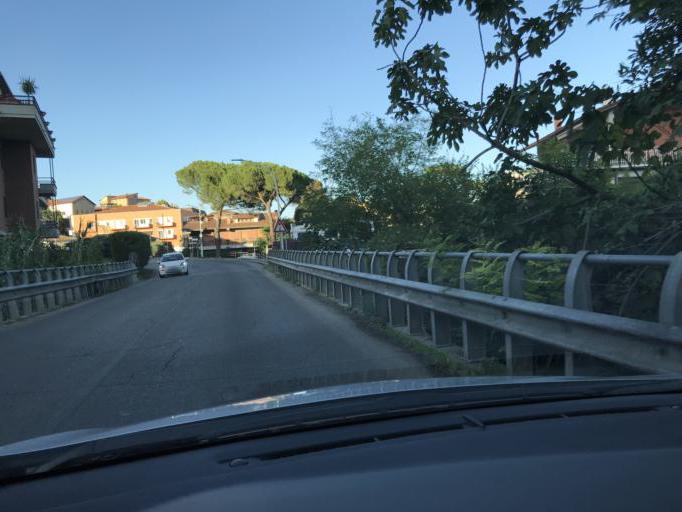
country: IT
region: Latium
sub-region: Provincia di Viterbo
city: Orte
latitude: 42.4559
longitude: 12.3866
